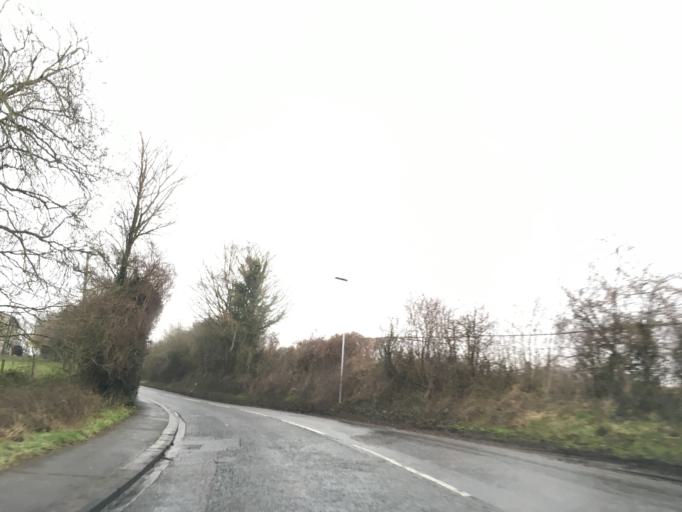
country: GB
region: England
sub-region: South Gloucestershire
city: Alveston
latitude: 51.5966
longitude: -2.5303
